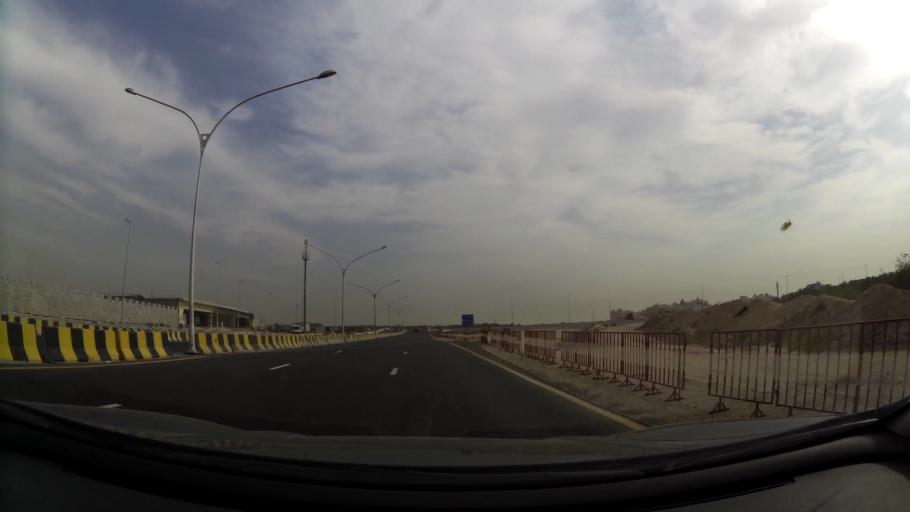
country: KW
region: Muhafazat al Jahra'
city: Al Jahra'
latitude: 29.3340
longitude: 47.7967
